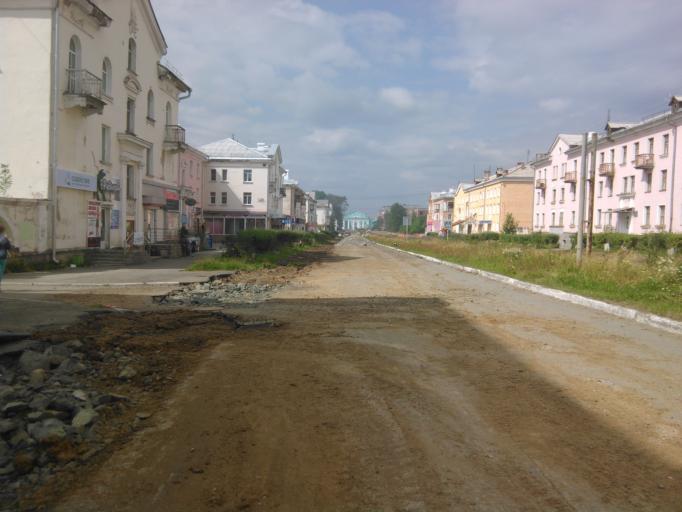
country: RU
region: Sverdlovsk
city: Krasnotur'insk
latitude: 59.7637
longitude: 60.1914
